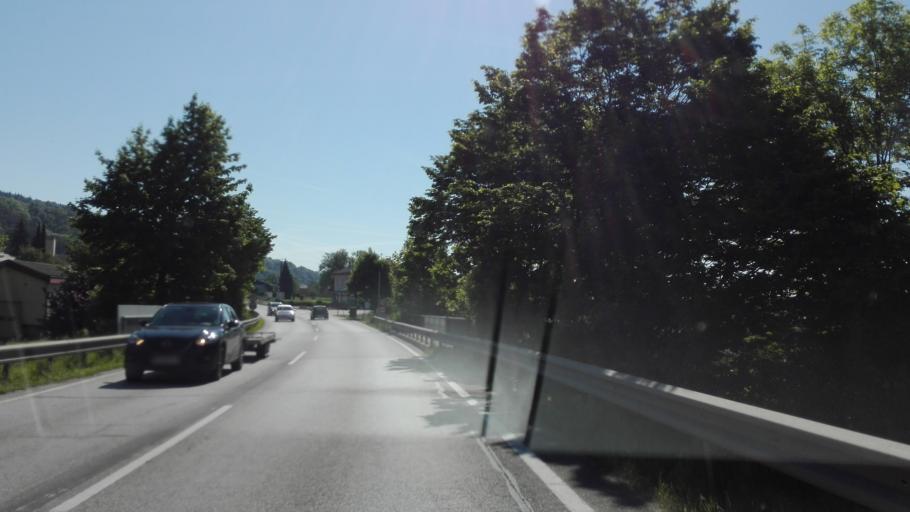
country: AT
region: Upper Austria
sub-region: Politischer Bezirk Urfahr-Umgebung
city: Feldkirchen an der Donau
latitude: 48.3619
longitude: 14.0288
